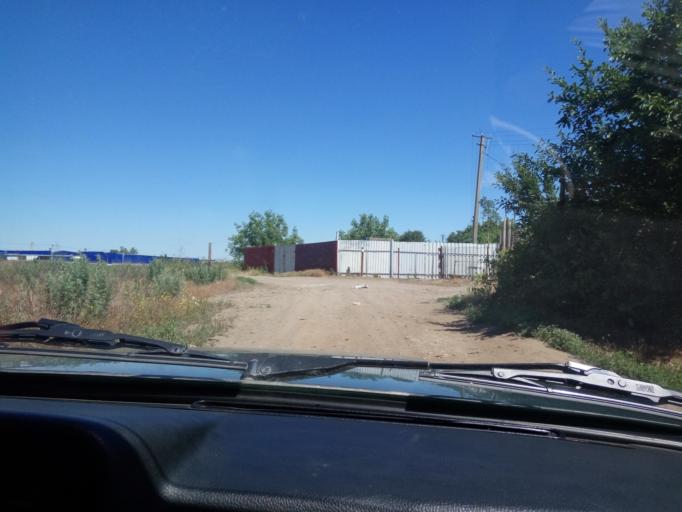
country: RU
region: Rostov
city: Bataysk
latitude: 47.0805
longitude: 39.7477
